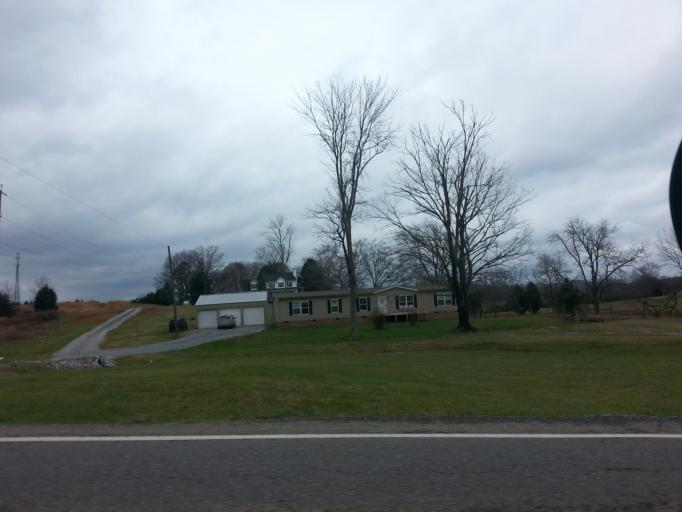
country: US
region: Tennessee
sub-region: Union County
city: Condon
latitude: 36.1160
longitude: -83.8768
